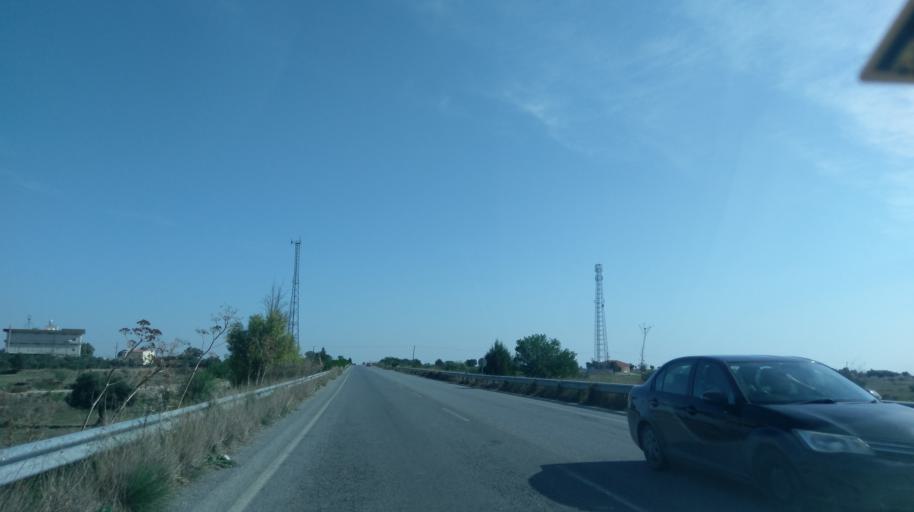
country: CY
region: Ammochostos
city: Lefkonoiko
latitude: 35.2595
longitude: 33.6600
